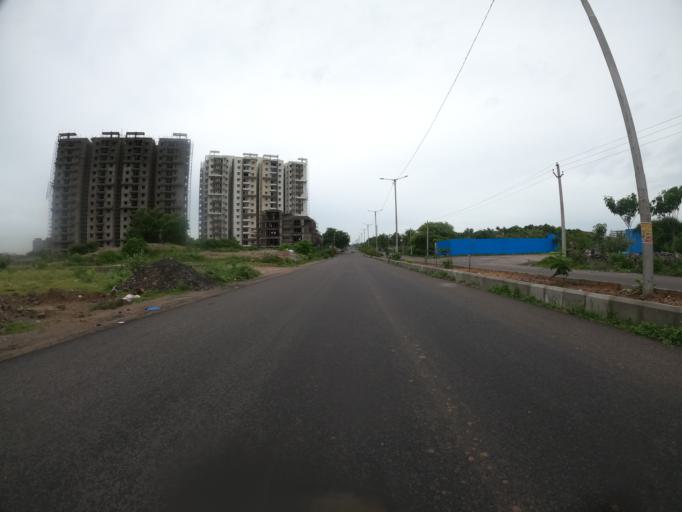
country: IN
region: Telangana
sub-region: Rangareddi
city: Kukatpalli
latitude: 17.4616
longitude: 78.3904
